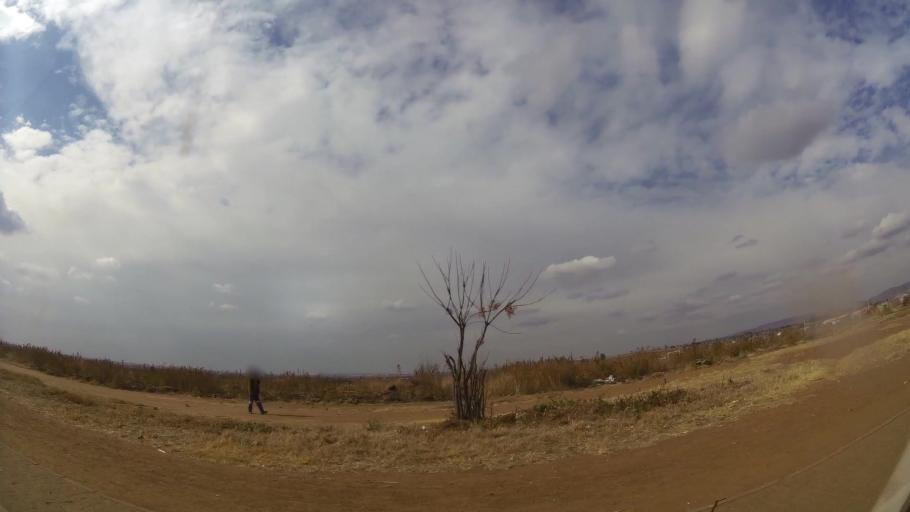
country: ZA
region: Gauteng
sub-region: Ekurhuleni Metropolitan Municipality
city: Germiston
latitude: -26.4005
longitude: 28.1632
